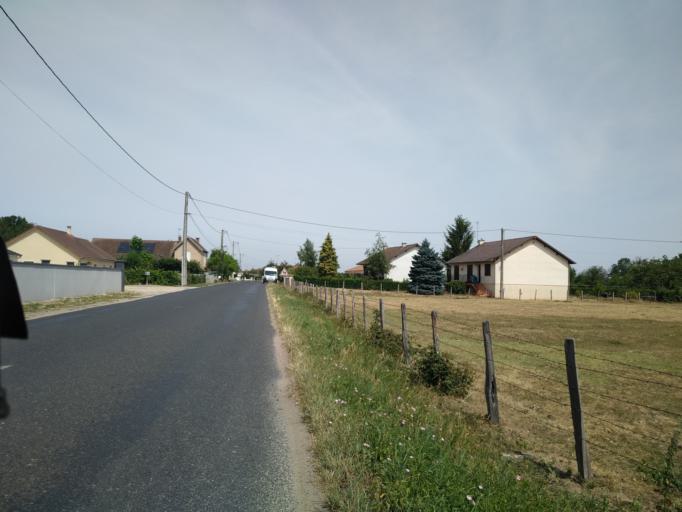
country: FR
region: Bourgogne
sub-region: Departement de Saone-et-Loire
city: Digoin
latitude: 46.4498
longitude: 3.9695
